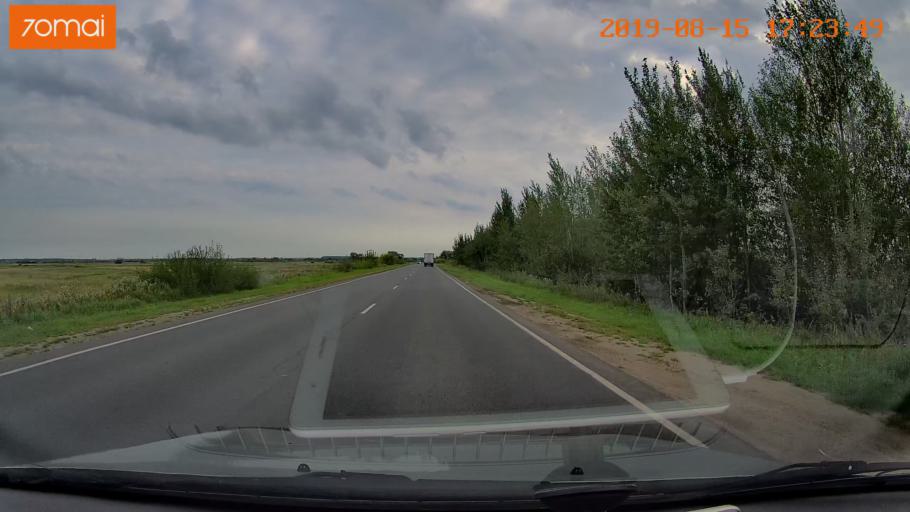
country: RU
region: Moskovskaya
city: Ashitkovo
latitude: 55.3962
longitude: 38.5548
